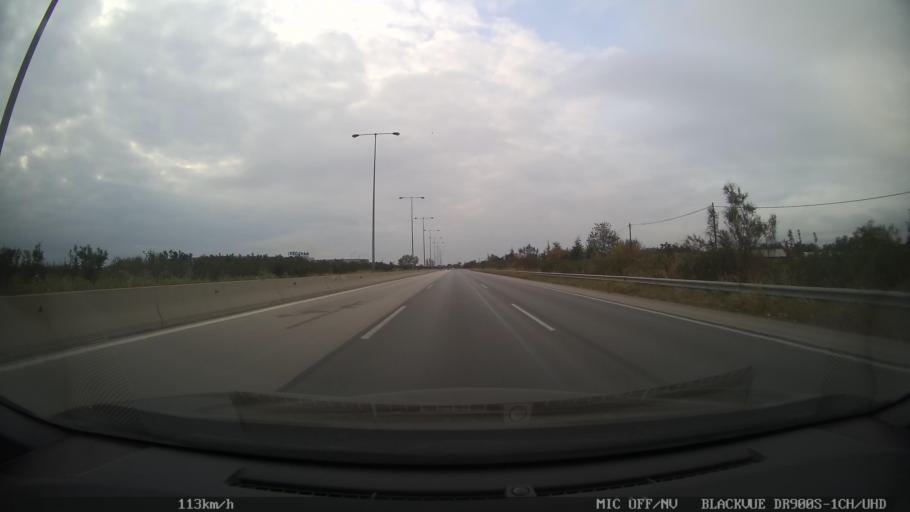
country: GR
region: Central Macedonia
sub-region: Nomos Thessalonikis
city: Nea Magnisia
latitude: 40.6793
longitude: 22.8324
